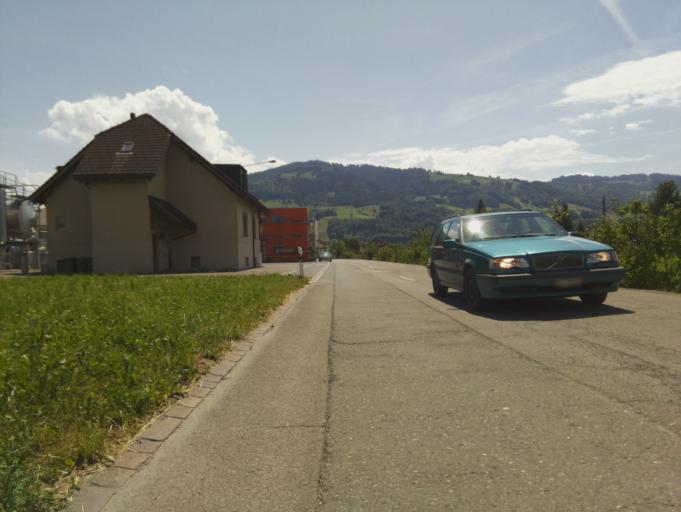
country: CH
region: Schwyz
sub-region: Bezirk March
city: Lachen
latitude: 47.1872
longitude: 8.8929
